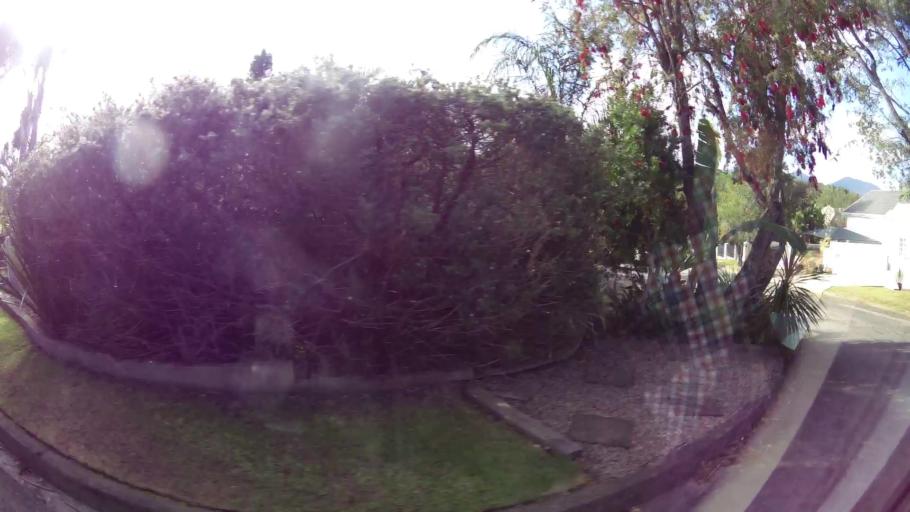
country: ZA
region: Western Cape
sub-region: Eden District Municipality
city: George
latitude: -33.9598
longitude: 22.4965
